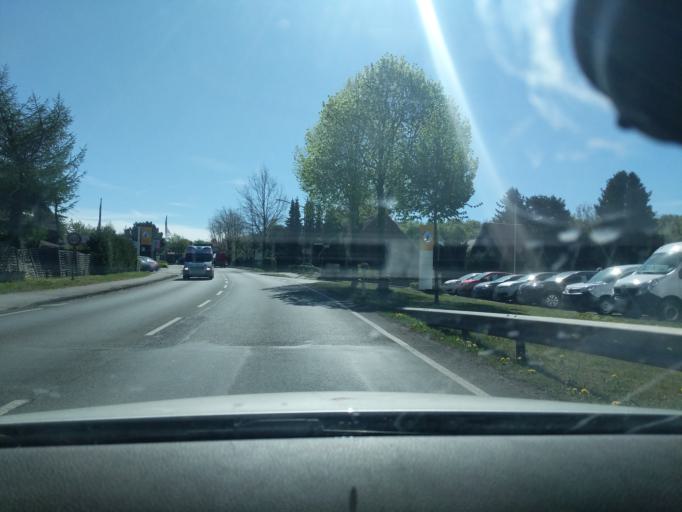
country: DE
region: Lower Saxony
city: Nottensdorf
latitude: 53.4843
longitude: 9.6202
